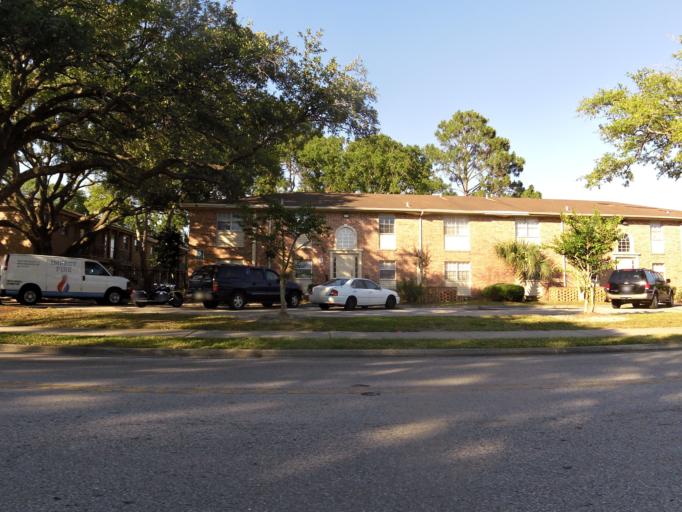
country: US
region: Florida
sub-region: Duval County
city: Jacksonville
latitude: 30.2494
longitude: -81.6226
